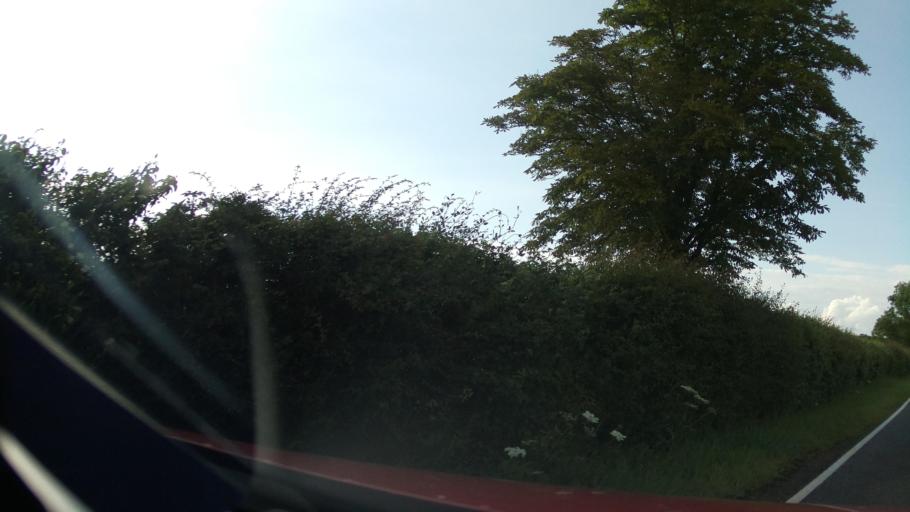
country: GB
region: England
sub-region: Lincolnshire
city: Great Gonerby
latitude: 53.0420
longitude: -0.6457
